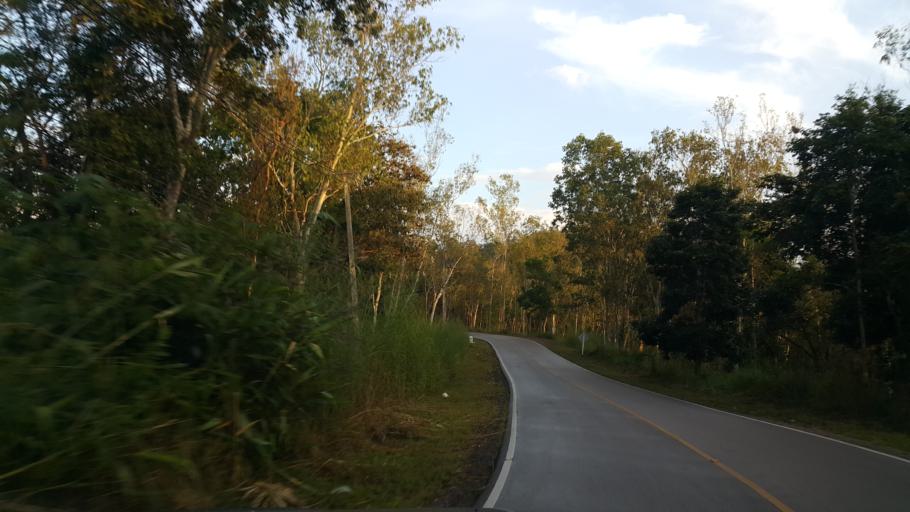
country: TH
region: Chiang Mai
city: Mae On
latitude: 18.7184
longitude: 99.2934
